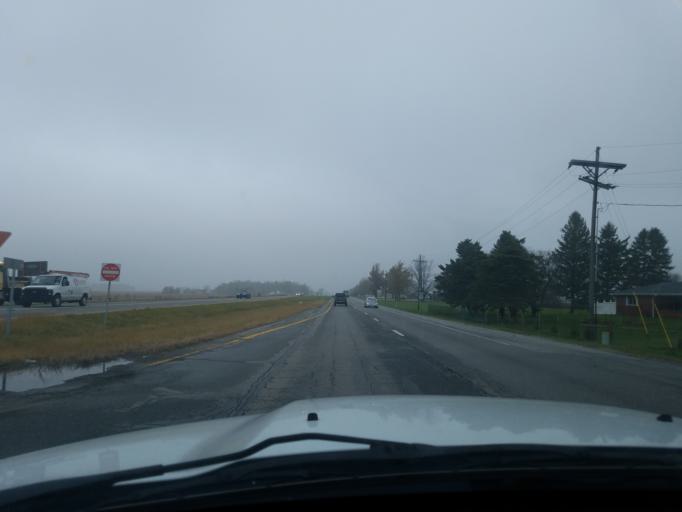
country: US
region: Indiana
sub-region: Howard County
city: Indian Heights
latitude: 40.3465
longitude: -86.1271
